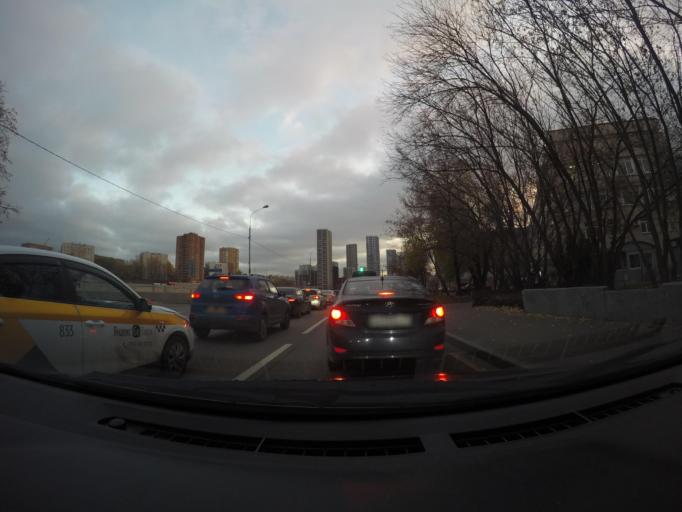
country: RU
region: Moscow
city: Taganskiy
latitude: 55.7238
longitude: 37.6563
